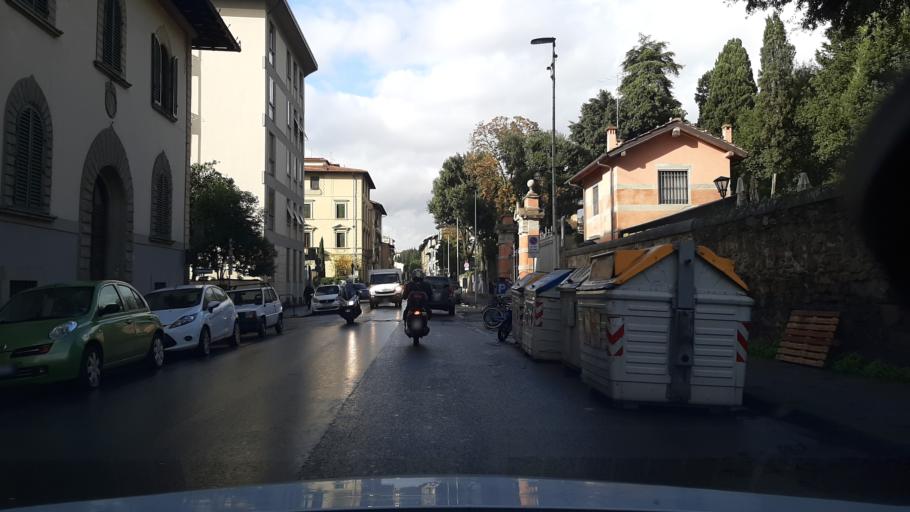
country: IT
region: Tuscany
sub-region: Province of Florence
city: Florence
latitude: 43.7891
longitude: 11.2568
